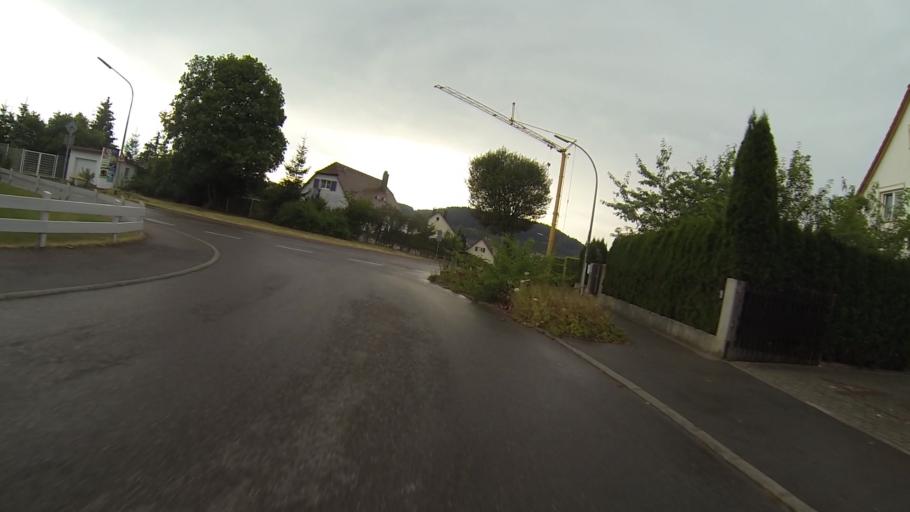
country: DE
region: Baden-Wuerttemberg
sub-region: Regierungsbezirk Stuttgart
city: Heidenheim an der Brenz
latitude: 48.7061
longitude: 10.1695
